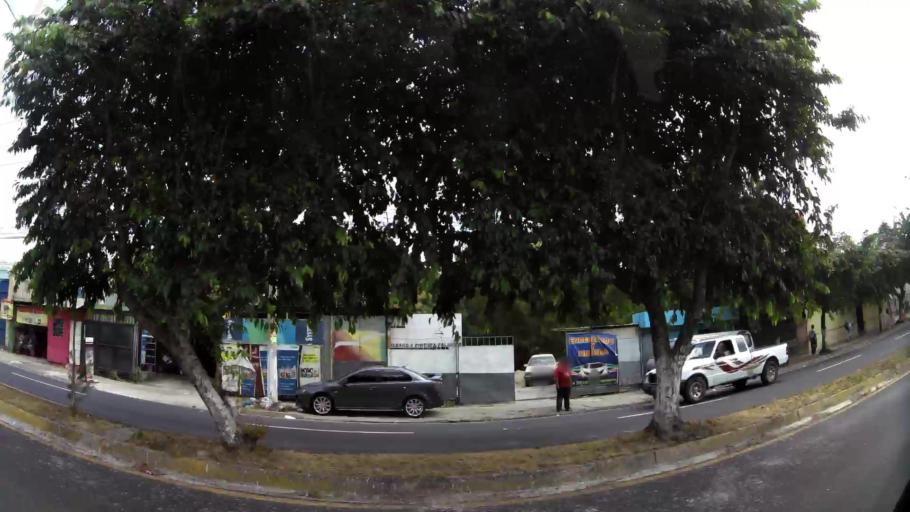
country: SV
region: San Salvador
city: Mejicanos
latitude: 13.7139
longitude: -89.2310
